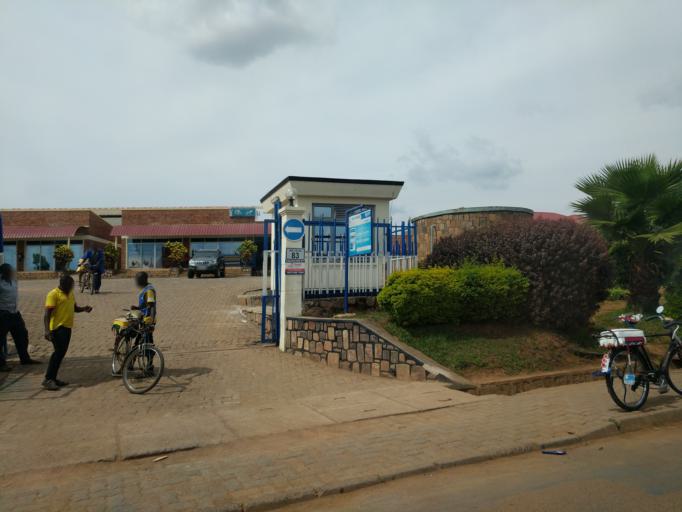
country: RW
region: Kigali
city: Kigali
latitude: -1.9708
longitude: 30.1258
